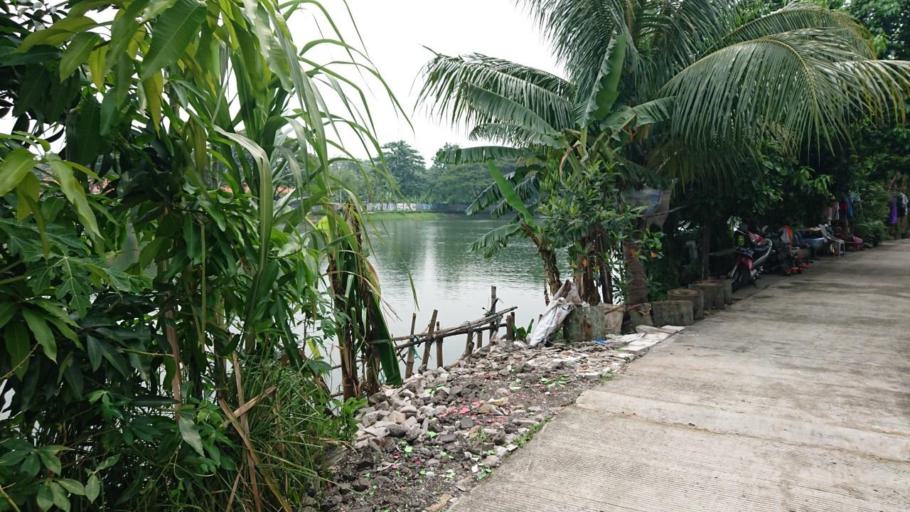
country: ID
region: West Java
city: Depok
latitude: -6.3553
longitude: 106.8686
